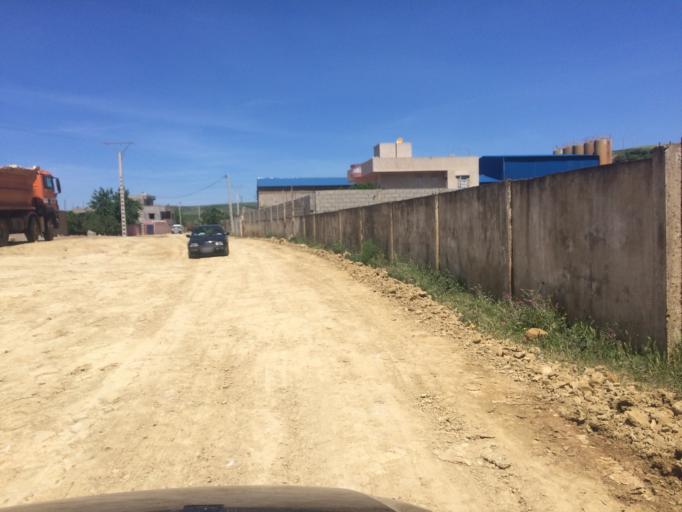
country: MA
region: Tanger-Tetouan
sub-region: Larache
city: Larache
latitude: 35.1914
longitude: -6.0818
